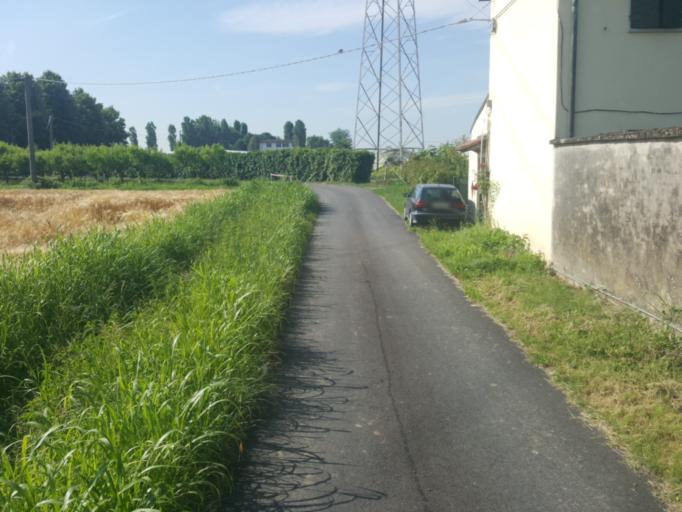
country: IT
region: Lombardy
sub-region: Provincia di Cremona
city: Crema
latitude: 45.3472
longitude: 9.6706
